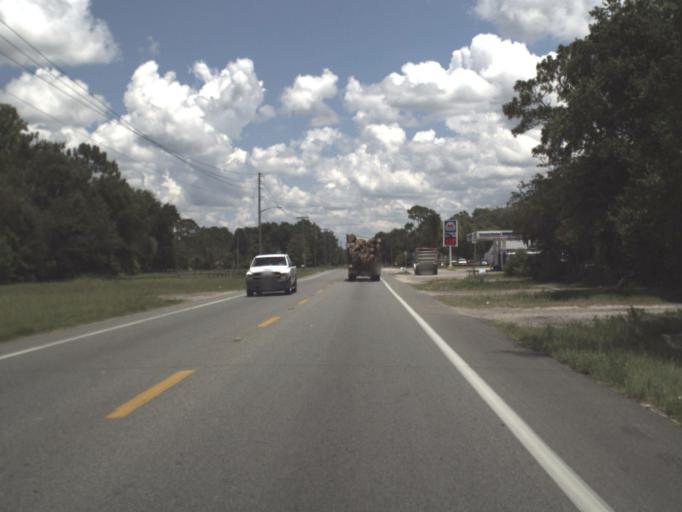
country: US
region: Florida
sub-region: Taylor County
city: Perry
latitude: 30.1078
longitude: -83.6004
